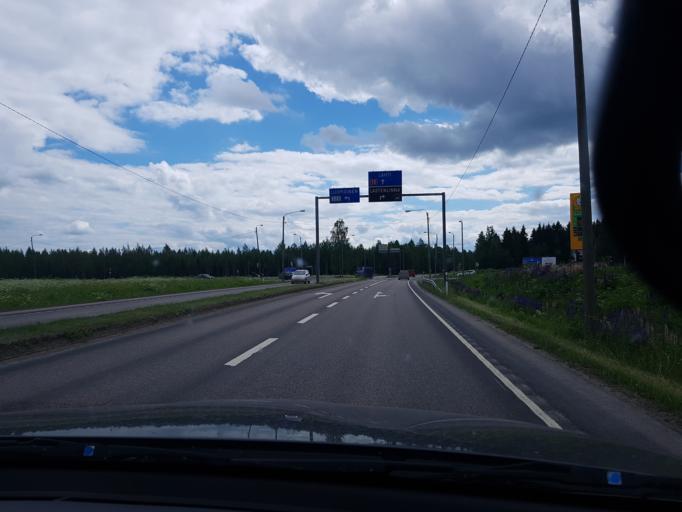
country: FI
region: Pirkanmaa
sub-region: Tampere
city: Paelkaene
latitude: 61.3315
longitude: 24.2868
